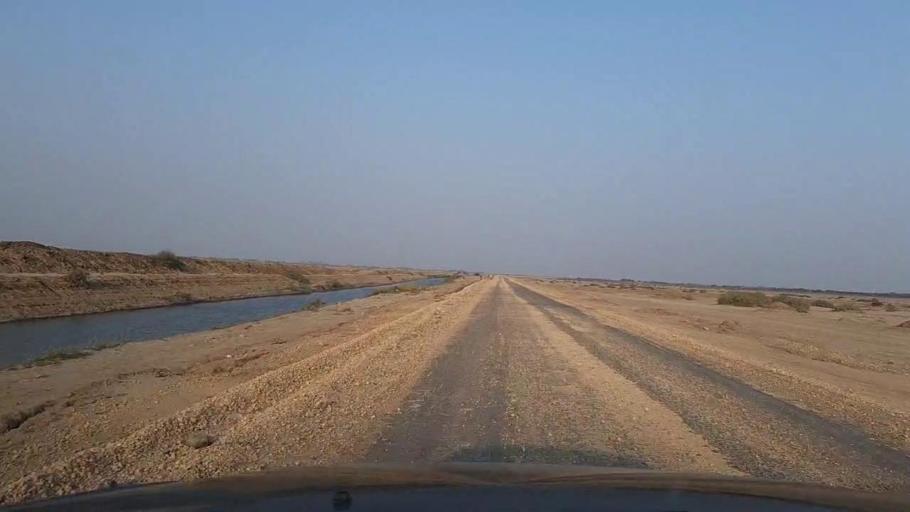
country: PK
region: Sindh
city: Mirpur Sakro
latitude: 24.4305
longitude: 67.7584
